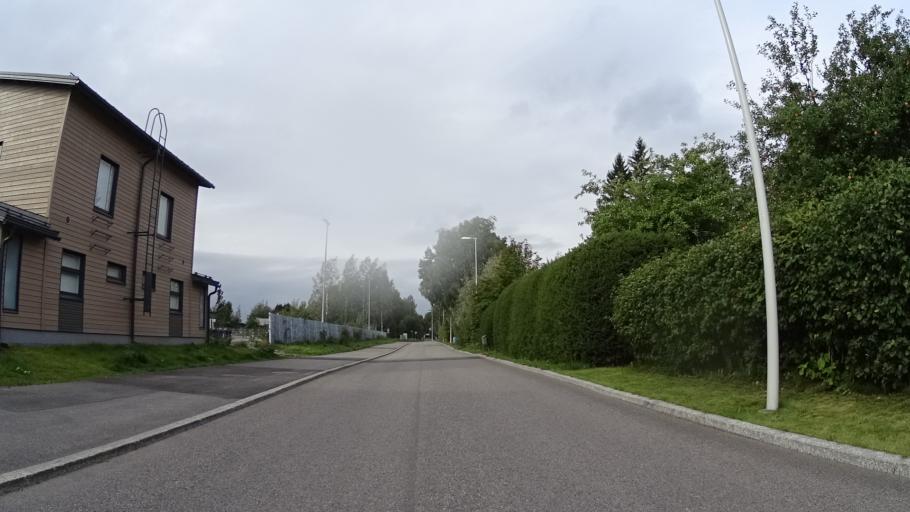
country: FI
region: Uusimaa
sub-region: Helsinki
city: Vantaa
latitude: 60.2950
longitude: 25.0079
